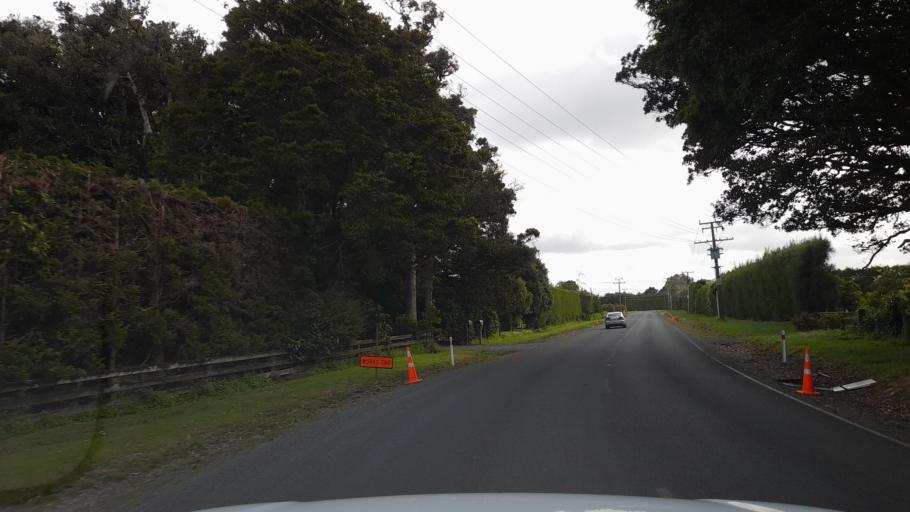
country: NZ
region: Northland
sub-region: Whangarei
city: Maungatapere
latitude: -35.7532
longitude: 174.2467
